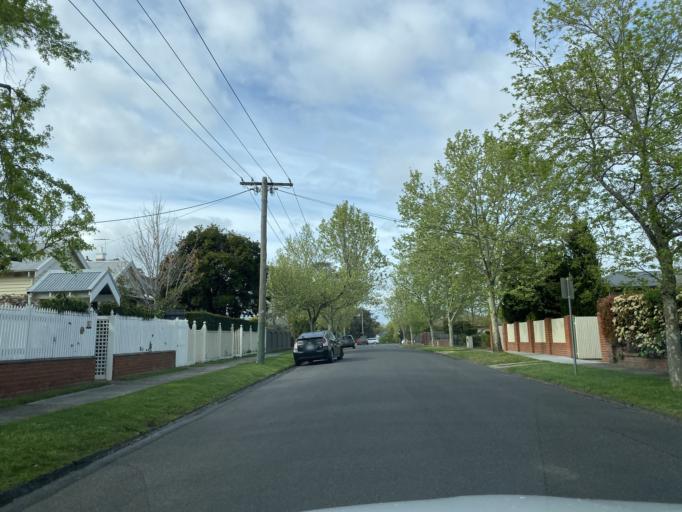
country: AU
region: Victoria
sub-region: Boroondara
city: Canterbury
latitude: -37.8332
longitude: 145.0853
